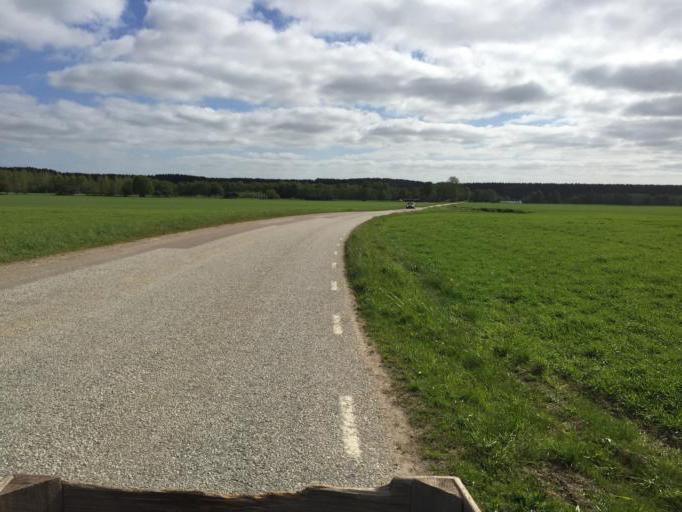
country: SE
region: Skane
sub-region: Sjobo Kommun
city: Blentarp
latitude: 55.6680
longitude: 13.6234
